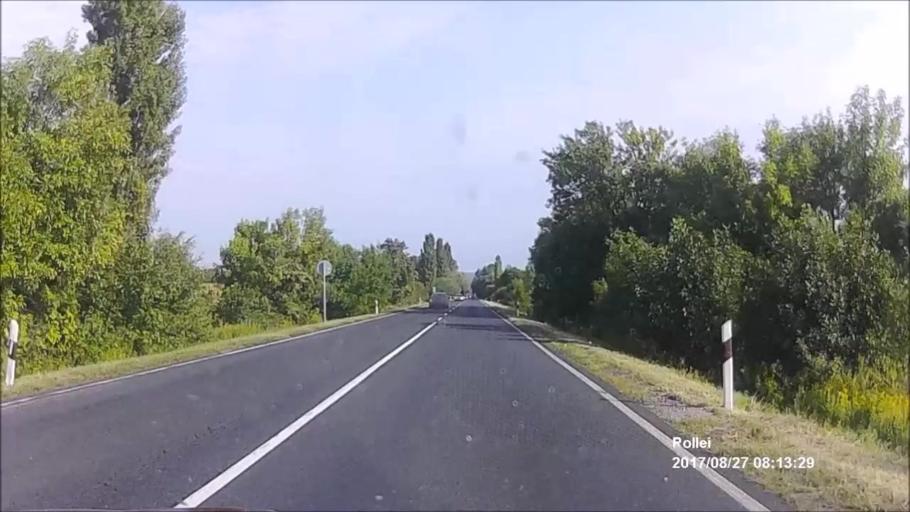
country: HU
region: Veszprem
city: Tapolca
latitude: 46.8456
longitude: 17.3711
